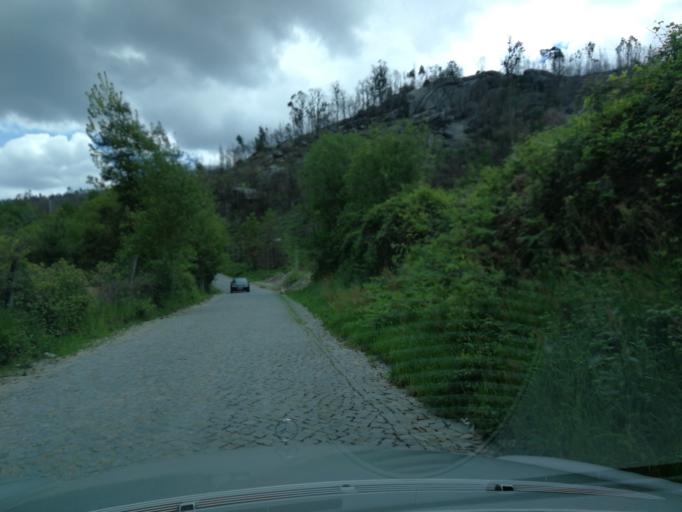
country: PT
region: Braga
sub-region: Braga
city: Braga
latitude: 41.5237
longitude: -8.4055
